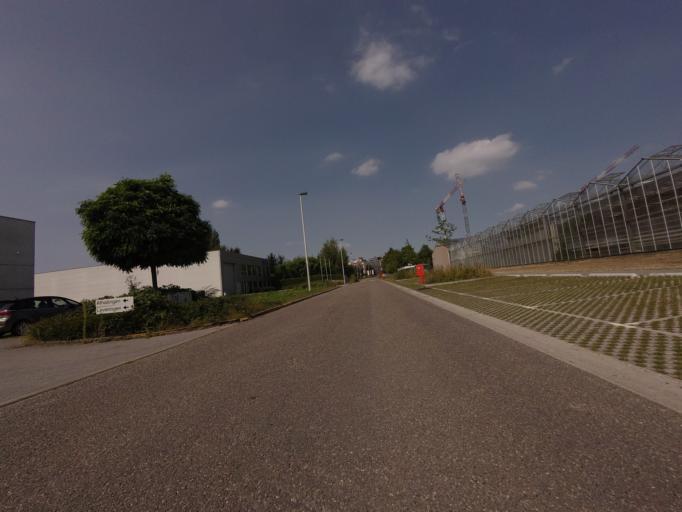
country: BE
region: Flanders
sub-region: Provincie Antwerpen
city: Aartselaar
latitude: 51.1599
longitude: 4.3900
